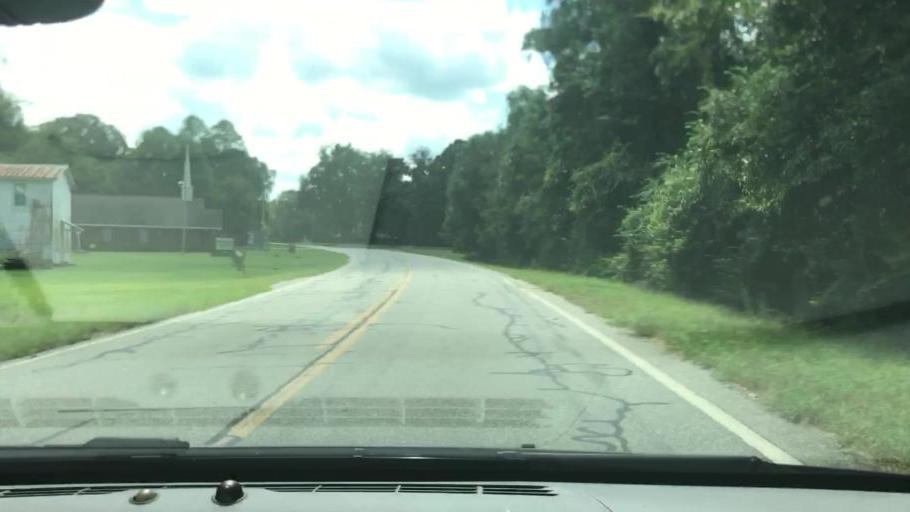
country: US
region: Georgia
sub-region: Quitman County
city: Georgetown
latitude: 32.0913
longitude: -85.0412
